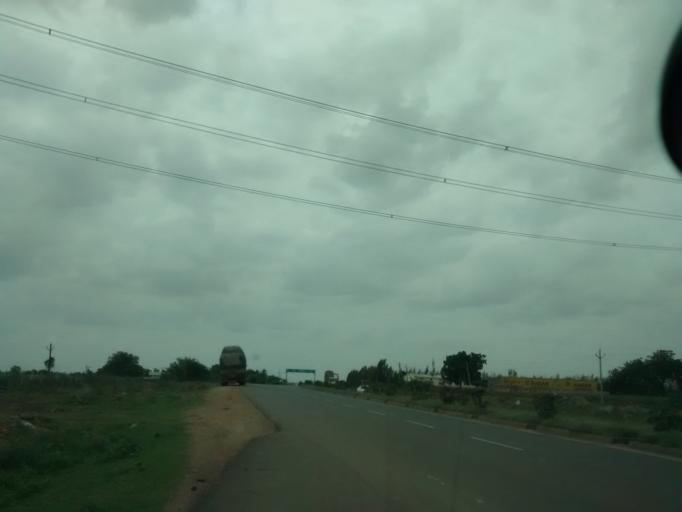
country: IN
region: Telangana
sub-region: Mahbubnagar
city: Alampur
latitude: 15.7238
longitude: 78.0017
